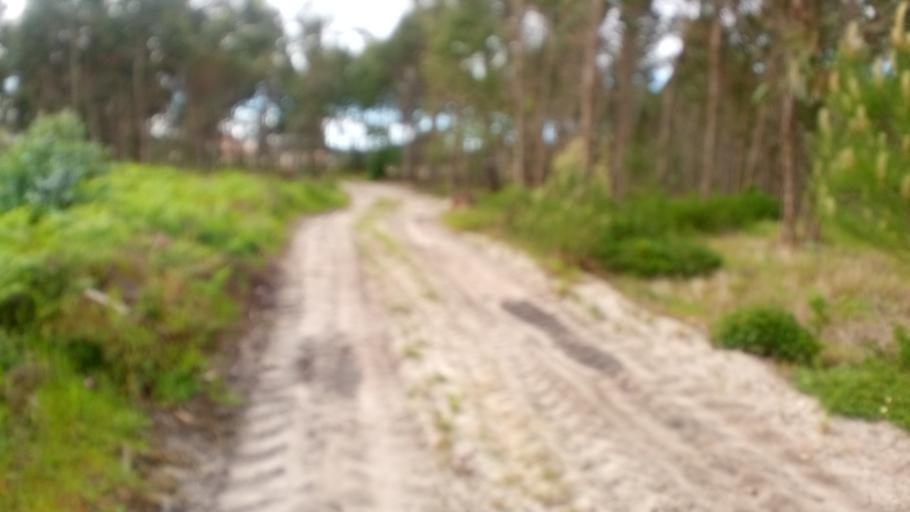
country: PT
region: Leiria
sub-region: Caldas da Rainha
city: Caldas da Rainha
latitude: 39.4513
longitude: -9.1695
